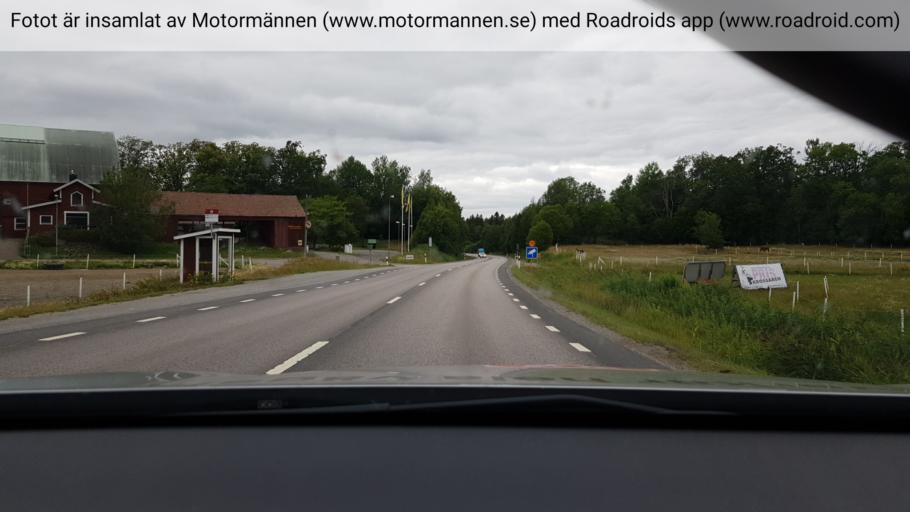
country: SE
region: Stockholm
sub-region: Nynashamns Kommun
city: Osmo
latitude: 58.9814
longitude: 17.8768
